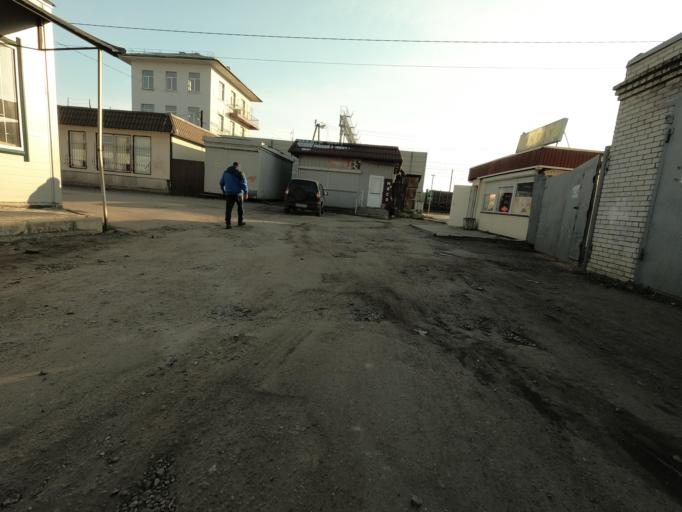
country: RU
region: Leningrad
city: Mga
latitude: 59.7565
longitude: 31.0590
